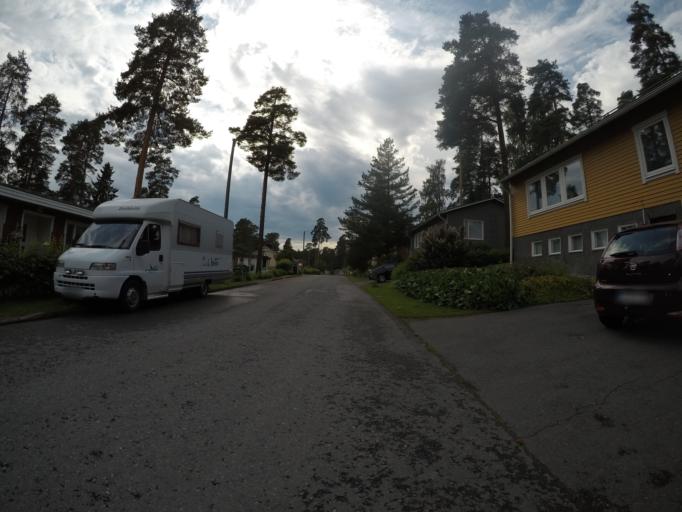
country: FI
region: Haeme
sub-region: Haemeenlinna
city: Haemeenlinna
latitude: 61.0143
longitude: 24.4718
